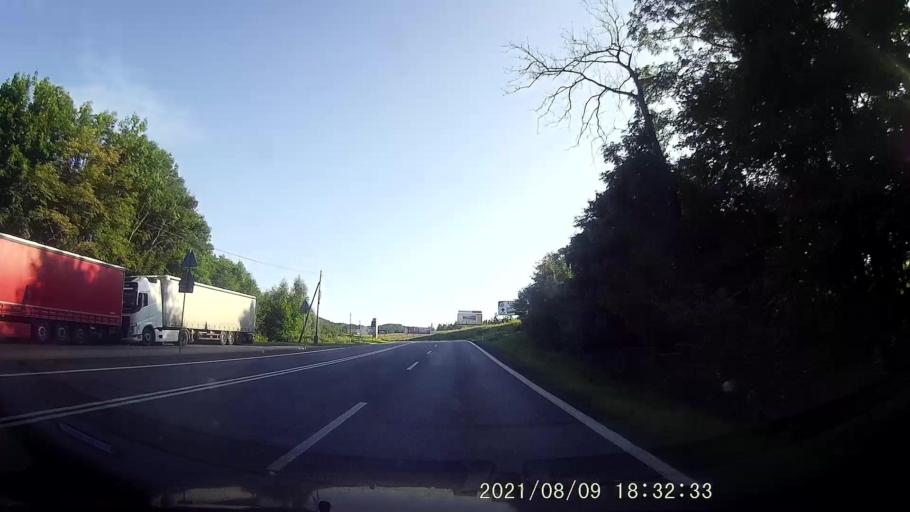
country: PL
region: Lower Silesian Voivodeship
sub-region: Powiat zabkowicki
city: Bardo
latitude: 50.4967
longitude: 16.7278
